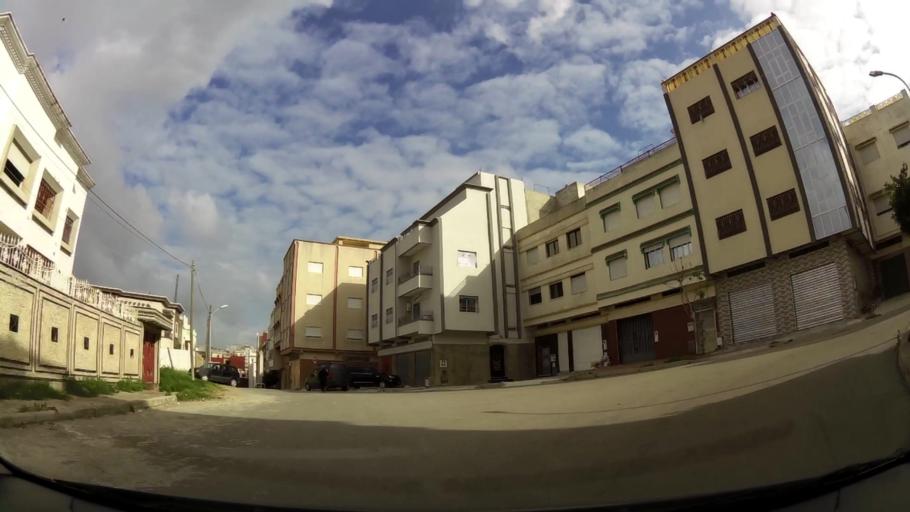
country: MA
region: Tanger-Tetouan
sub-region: Tanger-Assilah
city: Tangier
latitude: 35.7621
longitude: -5.8296
